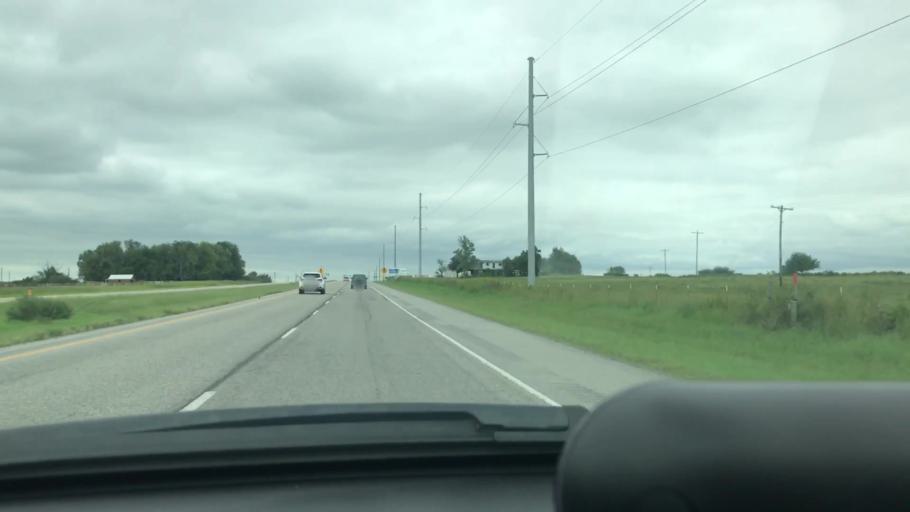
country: US
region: Oklahoma
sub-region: Wagoner County
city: Wagoner
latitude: 36.0125
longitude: -95.3686
